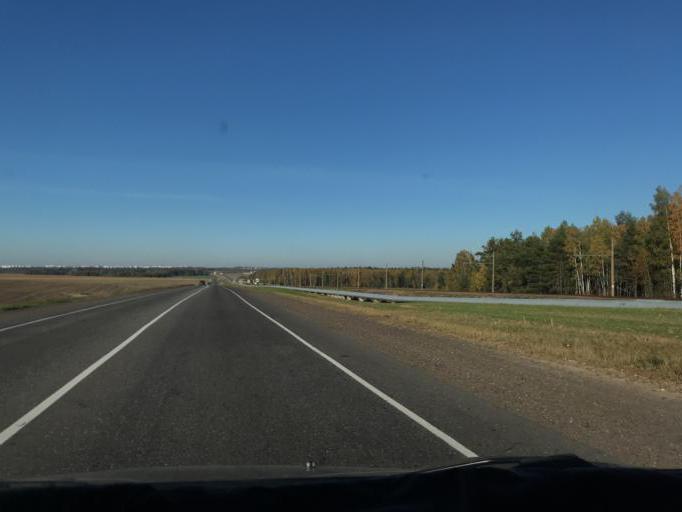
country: BY
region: Gomel
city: Mazyr
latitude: 51.9718
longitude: 29.2610
